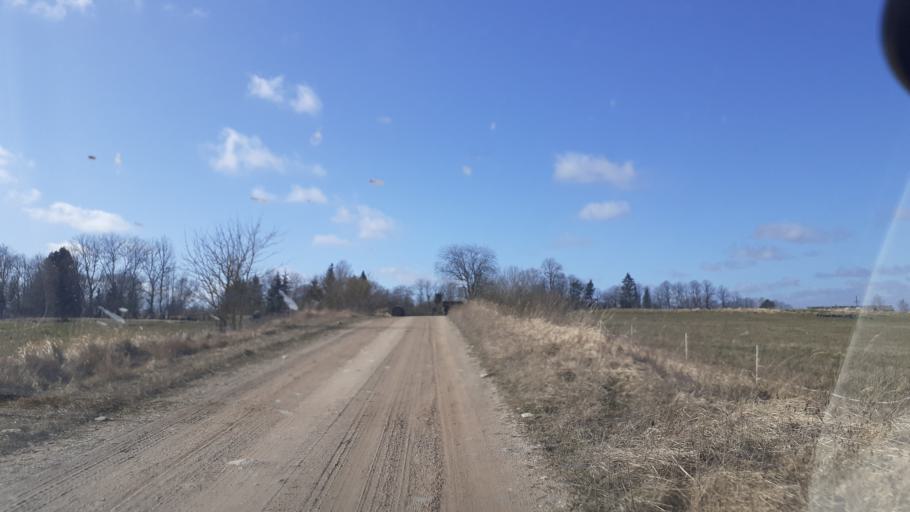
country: LV
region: Kuldigas Rajons
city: Kuldiga
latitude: 56.9335
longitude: 22.1625
